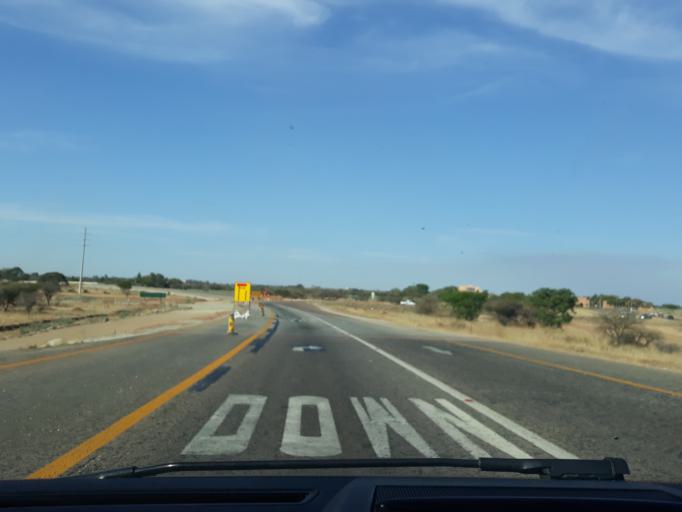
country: ZA
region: Limpopo
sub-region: Capricorn District Municipality
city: Polokwane
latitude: -23.9445
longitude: 29.4172
